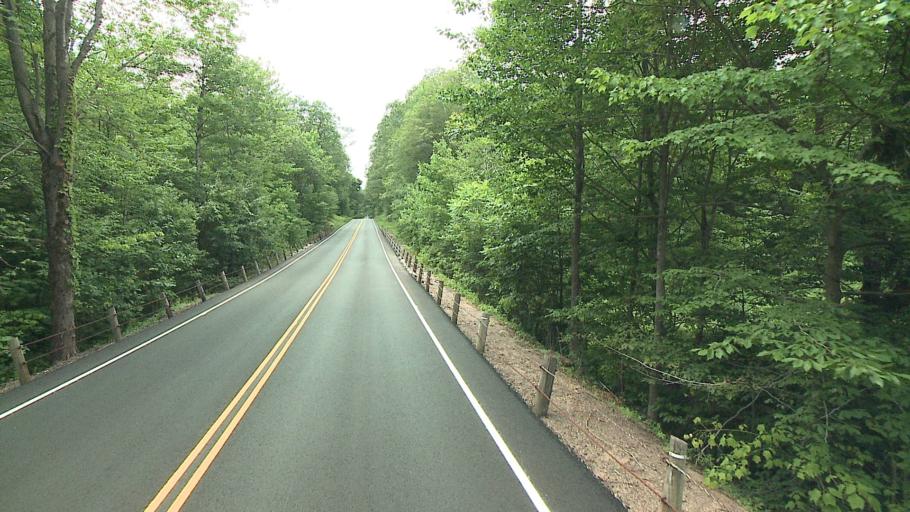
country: US
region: Massachusetts
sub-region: Hampden County
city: Granville
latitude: 42.0237
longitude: -72.8883
